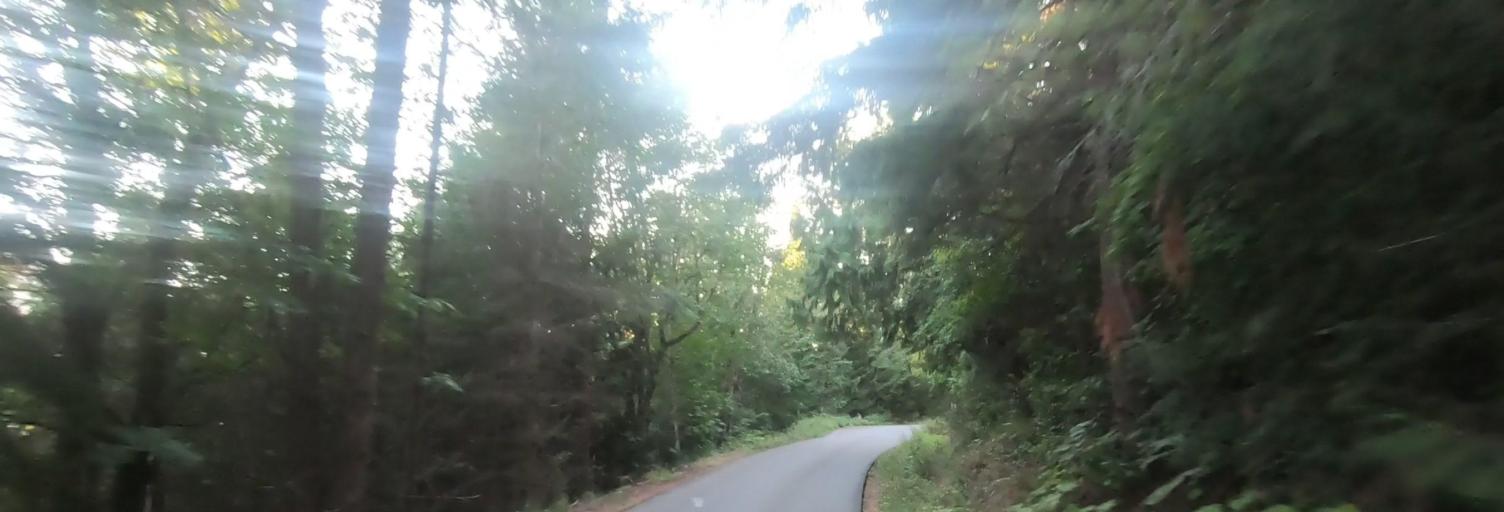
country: US
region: Washington
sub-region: Whatcom County
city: Peaceful Valley
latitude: 48.9063
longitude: -121.9632
